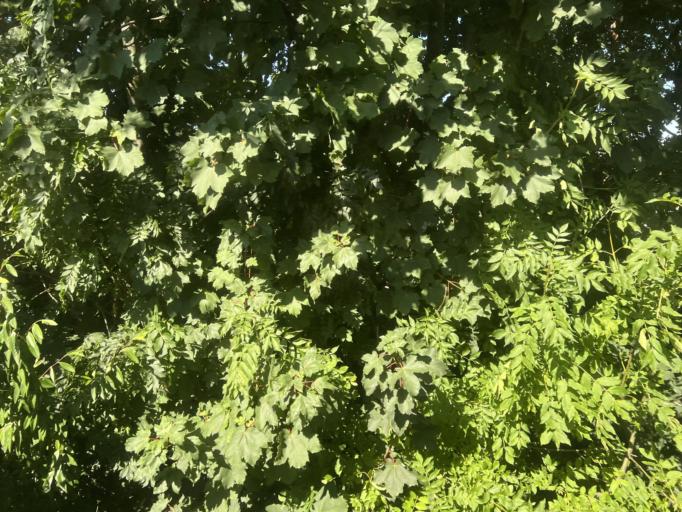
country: GB
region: England
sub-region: Lincolnshire
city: Boston
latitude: 52.9804
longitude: -0.0305
